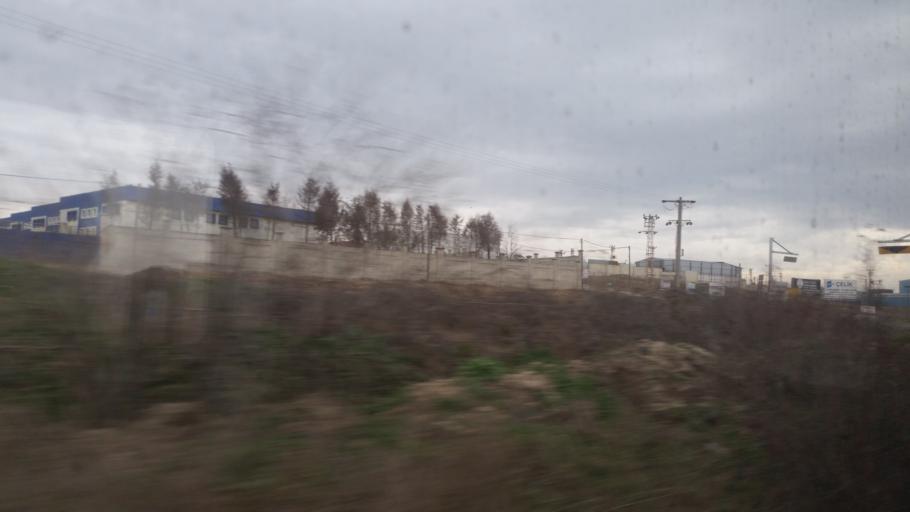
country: TR
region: Tekirdag
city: Velimese
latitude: 41.2667
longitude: 27.9364
